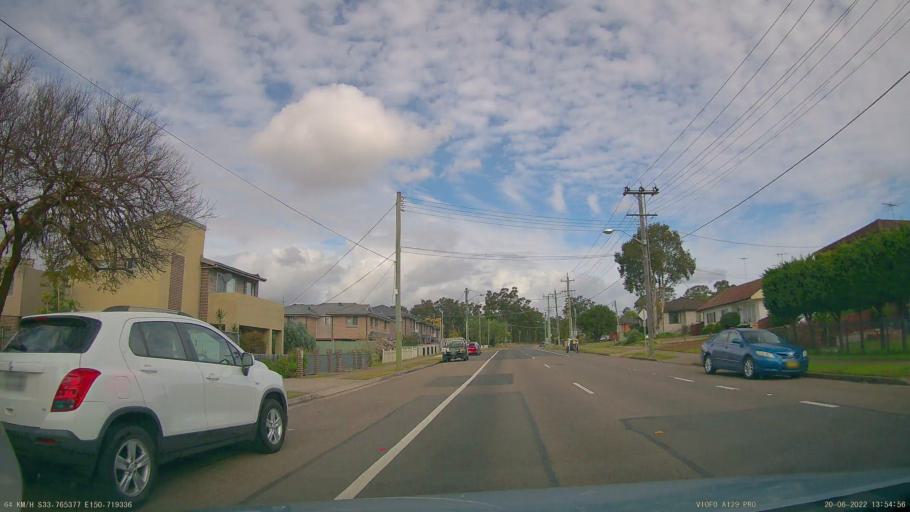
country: AU
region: New South Wales
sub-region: Penrith Municipality
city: Kingswood Park
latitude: -33.7656
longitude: 150.7193
